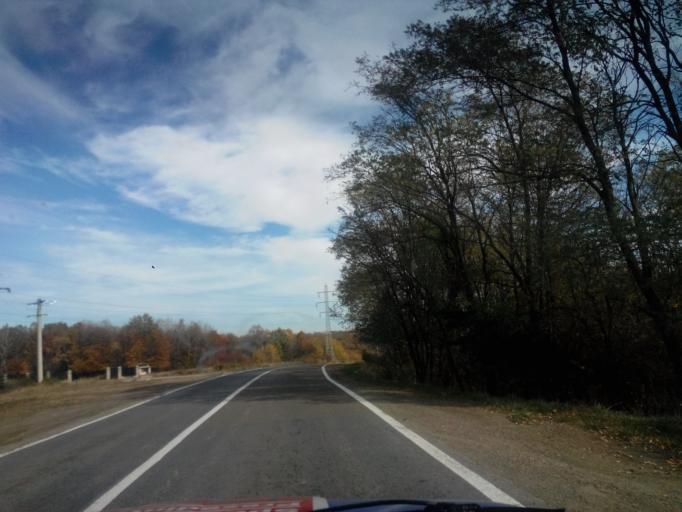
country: RO
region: Bacau
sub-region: Comuna Luizi-Calugara
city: Luizi-Calugara
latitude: 46.5065
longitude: 26.8085
